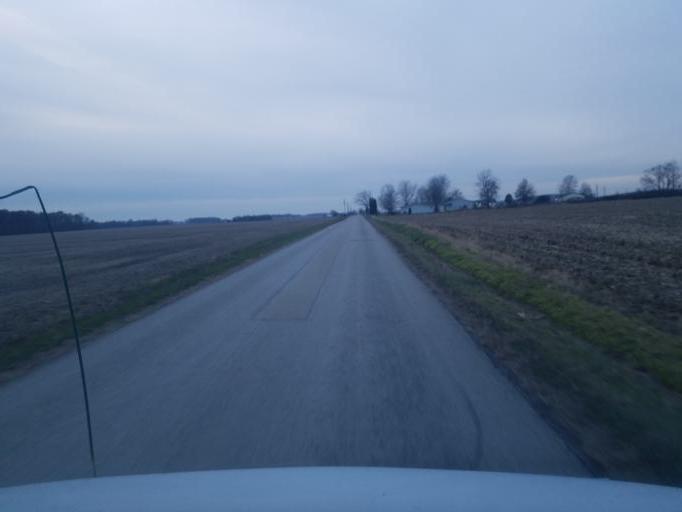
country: US
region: Indiana
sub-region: Adams County
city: Decatur
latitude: 40.7891
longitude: -84.9039
